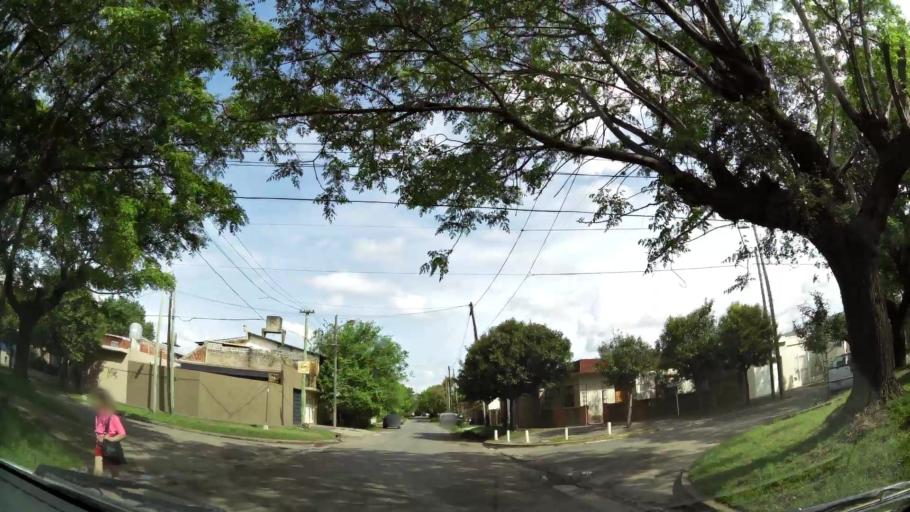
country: AR
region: Buenos Aires
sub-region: Partido de Quilmes
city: Quilmes
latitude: -34.7721
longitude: -58.2395
